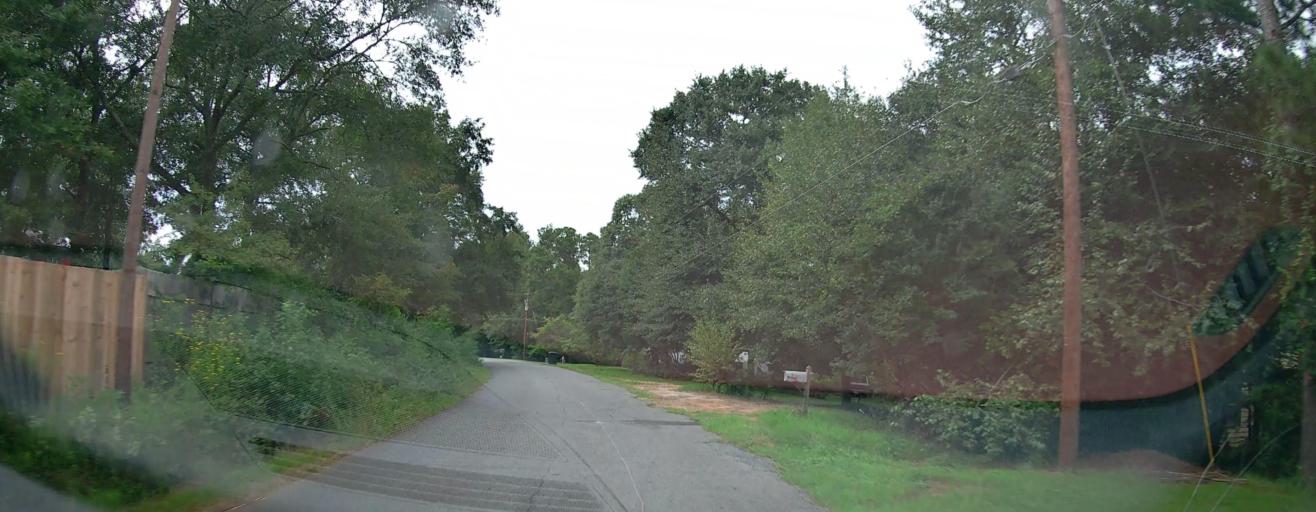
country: US
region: Georgia
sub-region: Peach County
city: Byron
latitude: 32.6770
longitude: -83.7132
